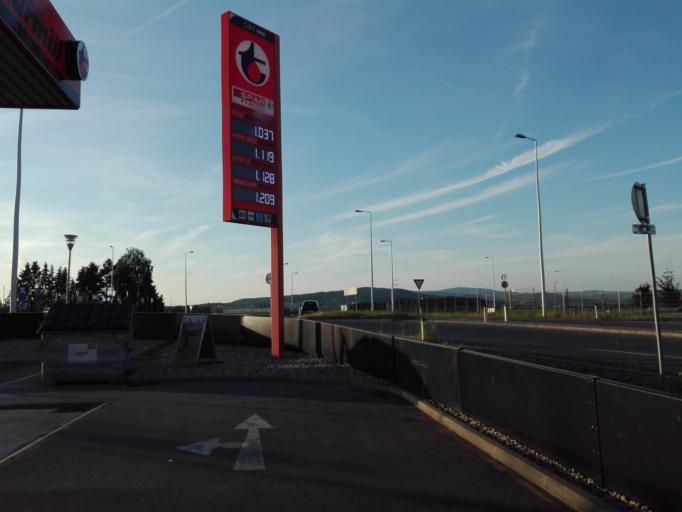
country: AT
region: Upper Austria
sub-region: Politischer Bezirk Linz-Land
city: Traun
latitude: 48.2437
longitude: 14.2231
